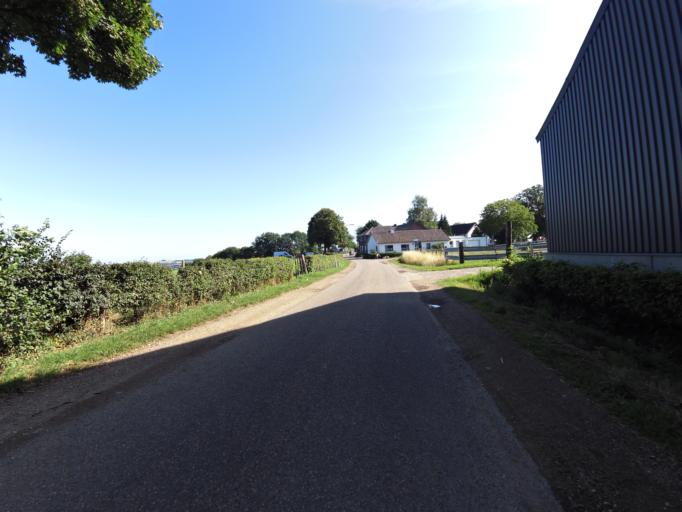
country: NL
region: Limburg
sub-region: Valkenburg aan de Geul
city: Schin op Geul
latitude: 50.8062
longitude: 5.8930
